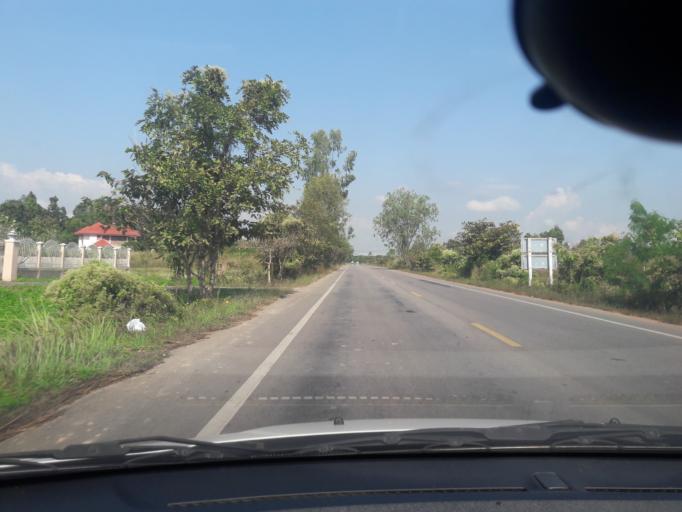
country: TH
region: Lampang
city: Lampang
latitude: 18.2146
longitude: 99.4931
